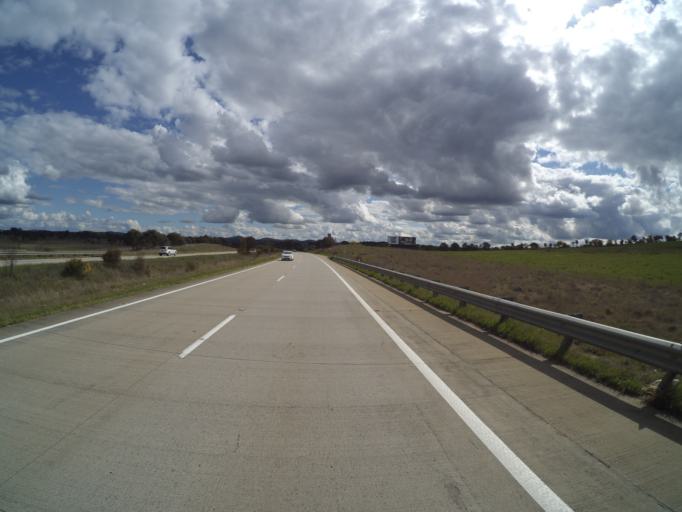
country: AU
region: New South Wales
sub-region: Yass Valley
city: Murrumbateman
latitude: -34.8005
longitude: 149.1421
